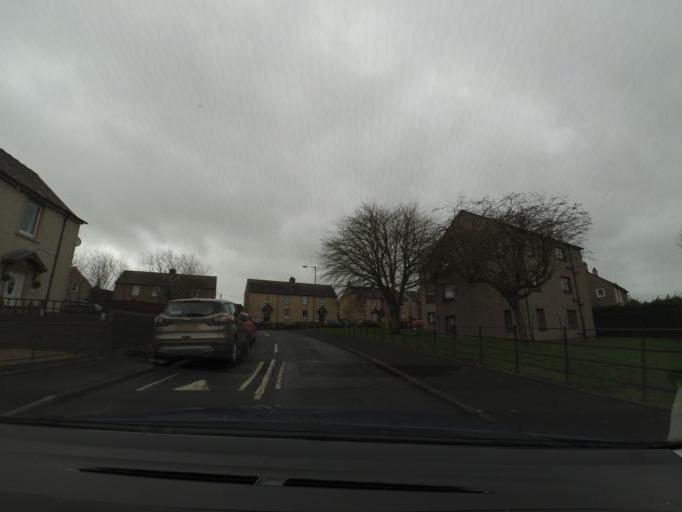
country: GB
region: Scotland
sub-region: The Scottish Borders
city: Hawick
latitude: 55.4392
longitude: -2.7731
